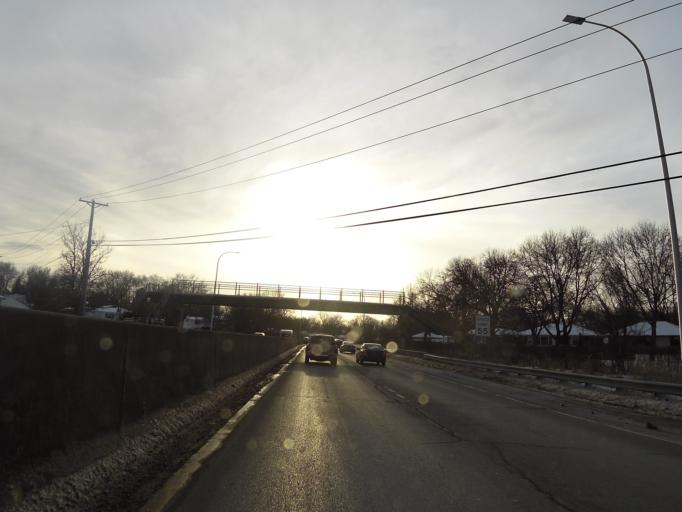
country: US
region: Minnesota
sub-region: Hennepin County
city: Richfield
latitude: 44.8923
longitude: -93.2546
